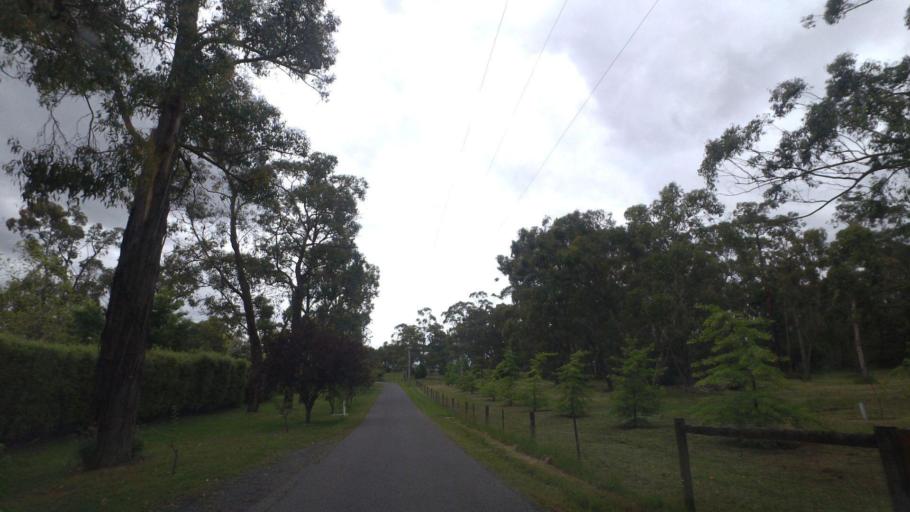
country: AU
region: Victoria
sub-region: Yarra Ranges
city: Mount Evelyn
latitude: -37.7552
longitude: 145.4210
